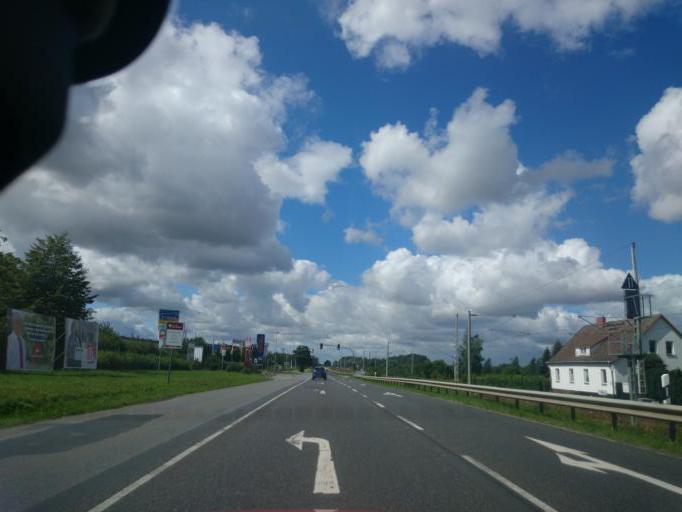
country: DE
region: Mecklenburg-Vorpommern
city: Stralsund
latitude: 54.3036
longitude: 13.0269
